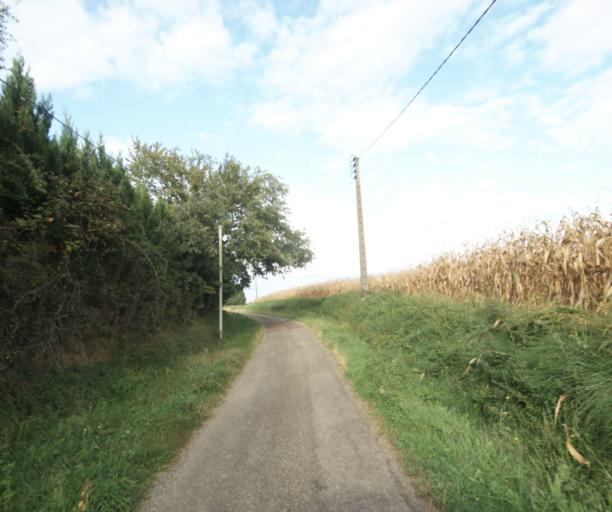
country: FR
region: Midi-Pyrenees
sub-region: Departement du Gers
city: Eauze
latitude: 43.8723
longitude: 0.0909
